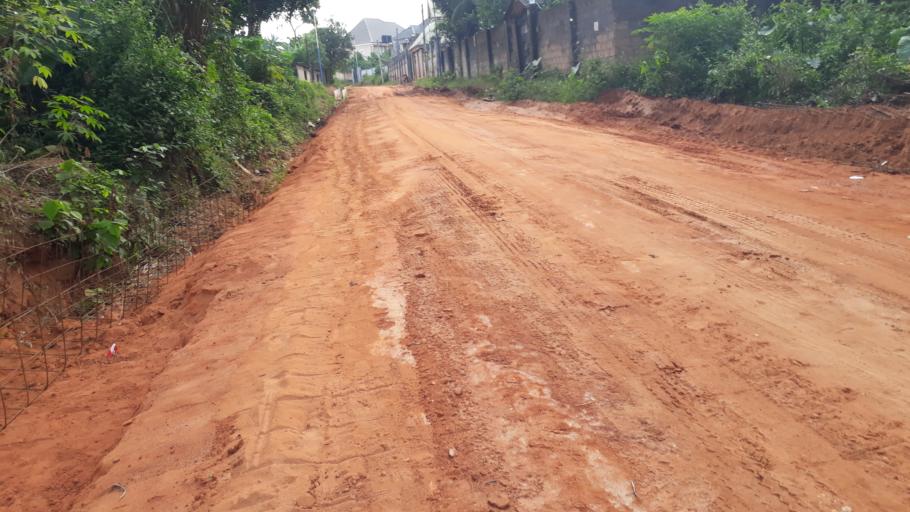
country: NG
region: Imo
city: Ihuo
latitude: 5.5718
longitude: 7.2640
